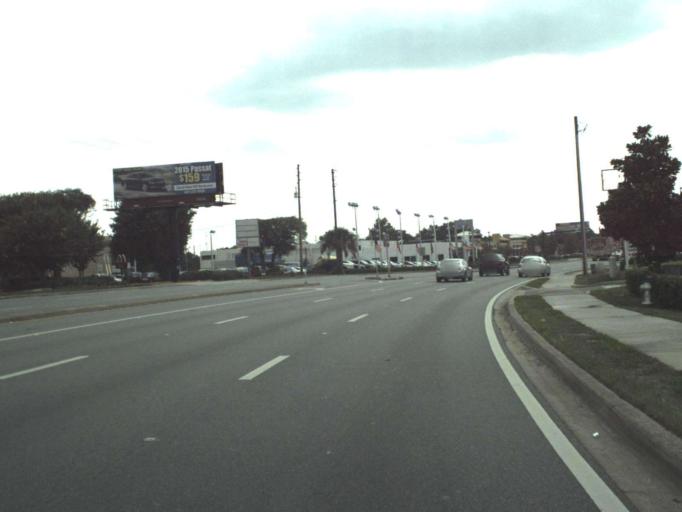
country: US
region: Florida
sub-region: Orange County
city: Fairview Shores
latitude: 28.6060
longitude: -81.3952
